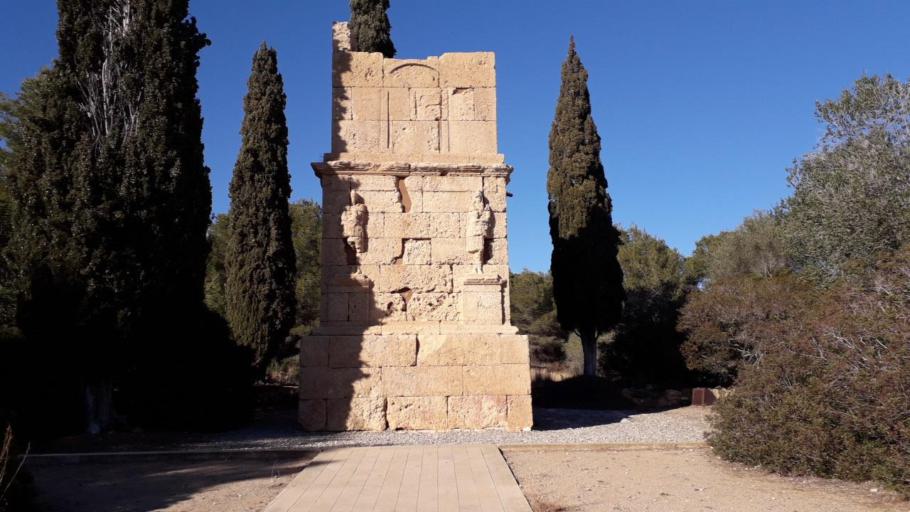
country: ES
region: Catalonia
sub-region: Provincia de Tarragona
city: el Catllar
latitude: 41.1319
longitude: 1.3190
